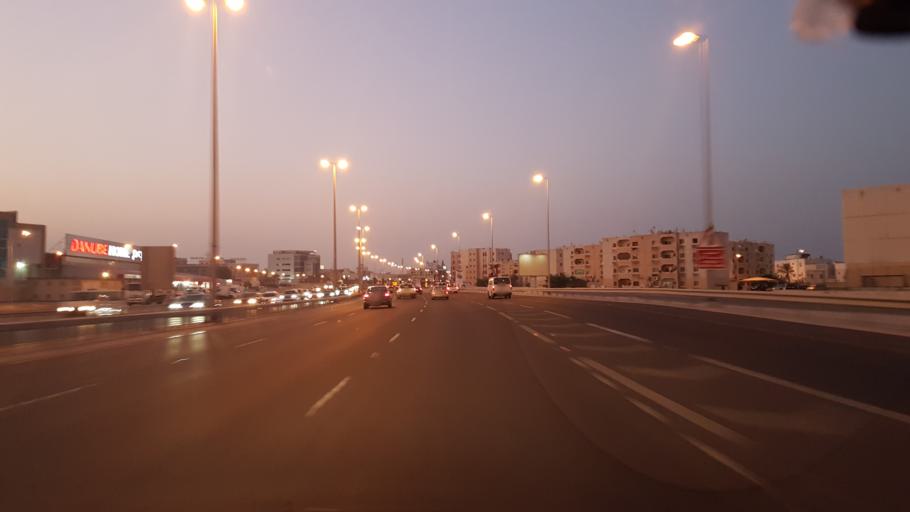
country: BH
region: Northern
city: Madinat `Isa
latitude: 26.1773
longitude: 50.5400
